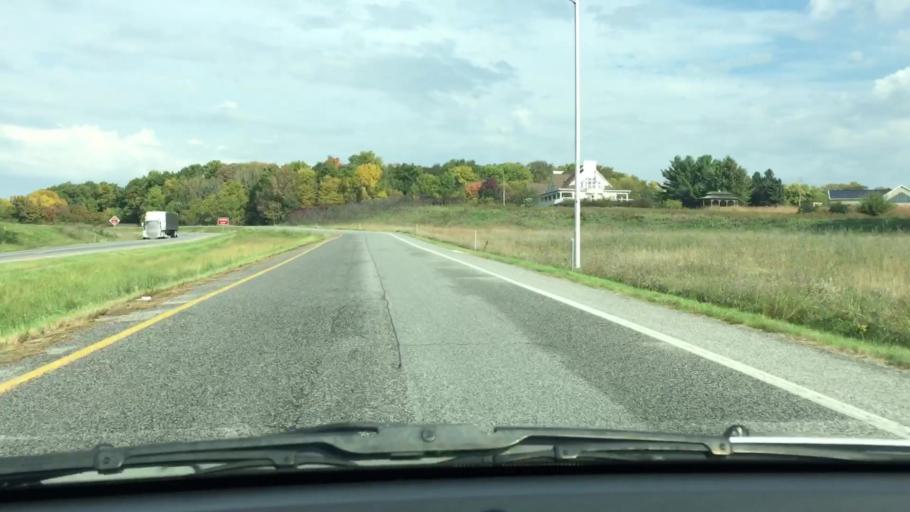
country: US
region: Iowa
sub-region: Scott County
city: Le Claire
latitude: 41.5854
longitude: -90.3658
